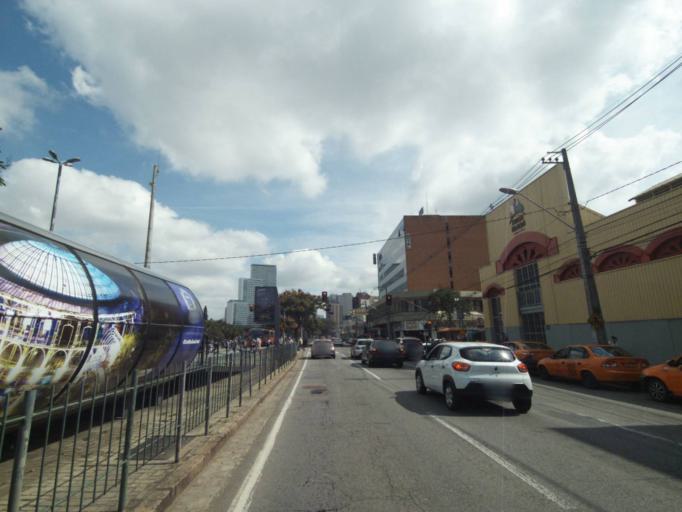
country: BR
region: Parana
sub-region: Curitiba
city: Curitiba
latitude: -25.4356
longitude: -49.2566
